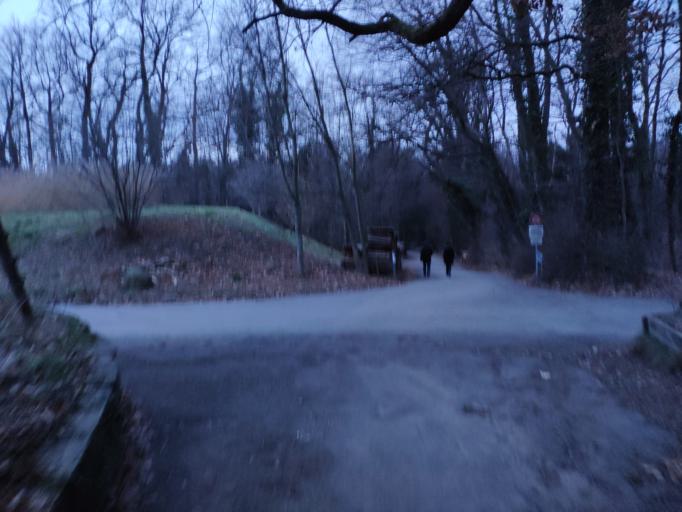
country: DE
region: Baden-Wuerttemberg
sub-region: Freiburg Region
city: Inzlingen
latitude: 47.5902
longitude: 7.6738
